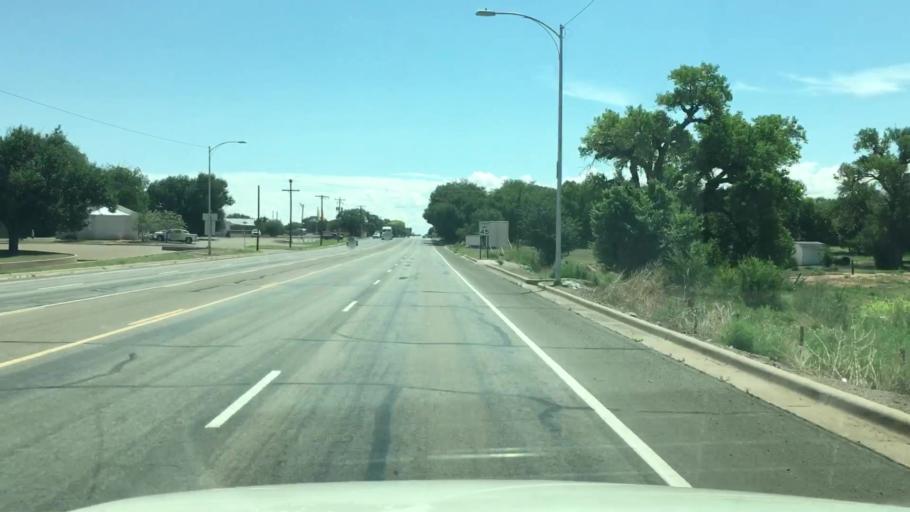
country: US
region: New Mexico
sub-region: De Baca County
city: Fort Sumner
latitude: 34.4684
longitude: -104.2353
